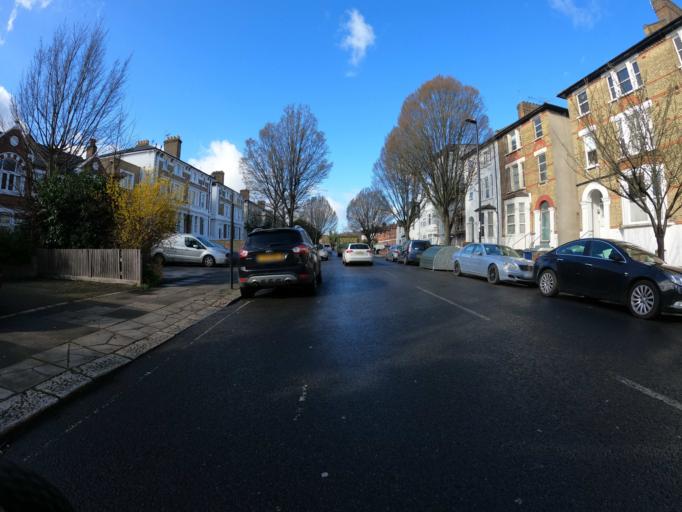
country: GB
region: England
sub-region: Greater London
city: Ealing
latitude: 51.5147
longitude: -0.3209
